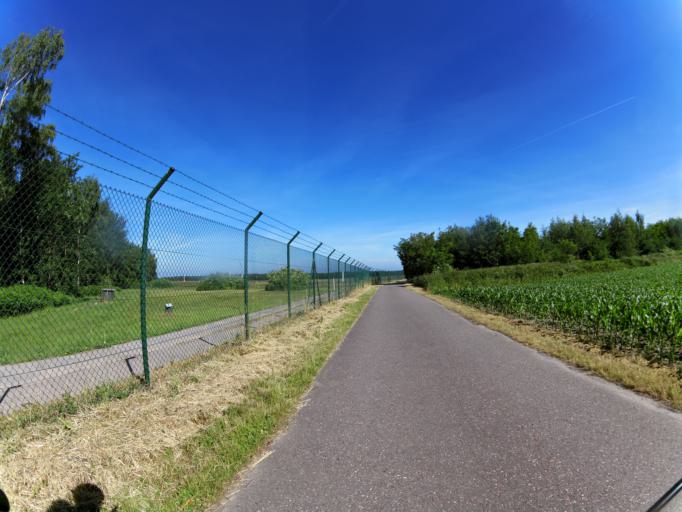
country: DE
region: North Rhine-Westphalia
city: Geilenkirchen
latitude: 50.9581
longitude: 6.0676
